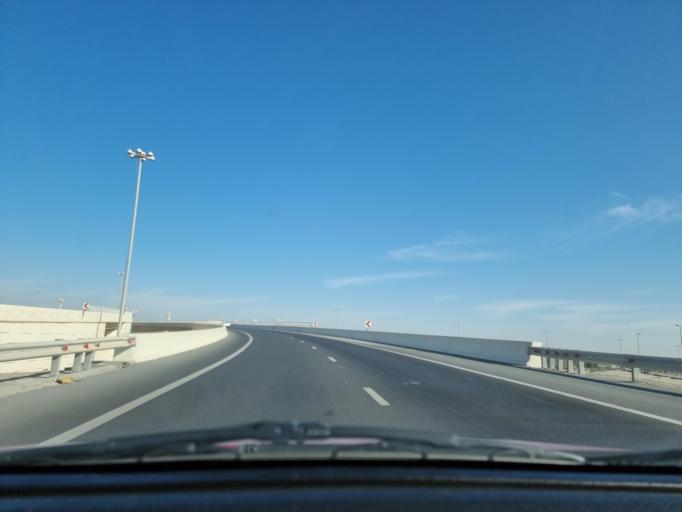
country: AE
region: Abu Dhabi
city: Abu Dhabi
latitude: 24.4133
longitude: 54.7175
